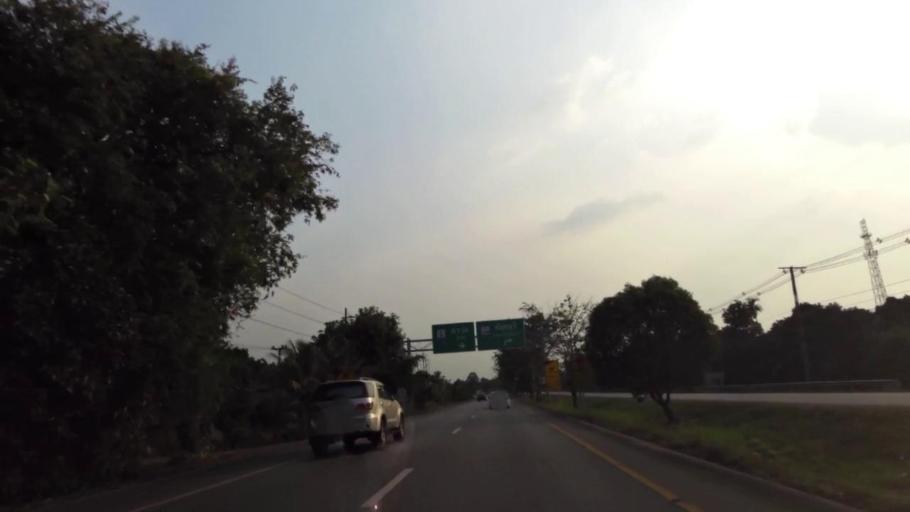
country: TH
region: Chanthaburi
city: Chanthaburi
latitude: 12.5326
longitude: 102.1574
